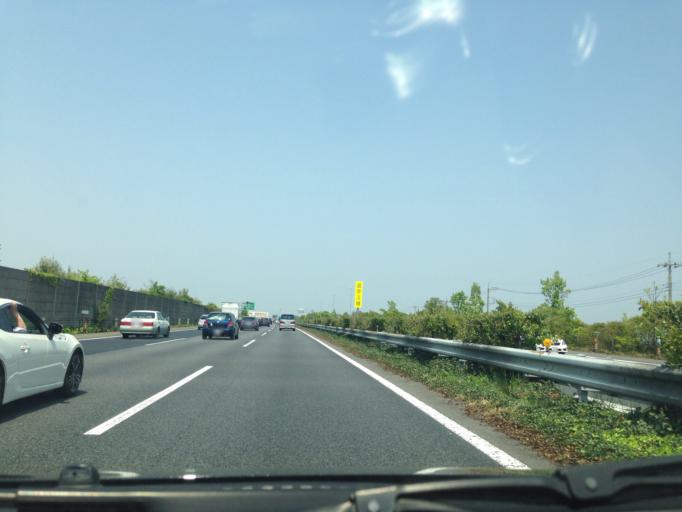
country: JP
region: Saitama
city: Hanyu
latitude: 36.1965
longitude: 139.5807
